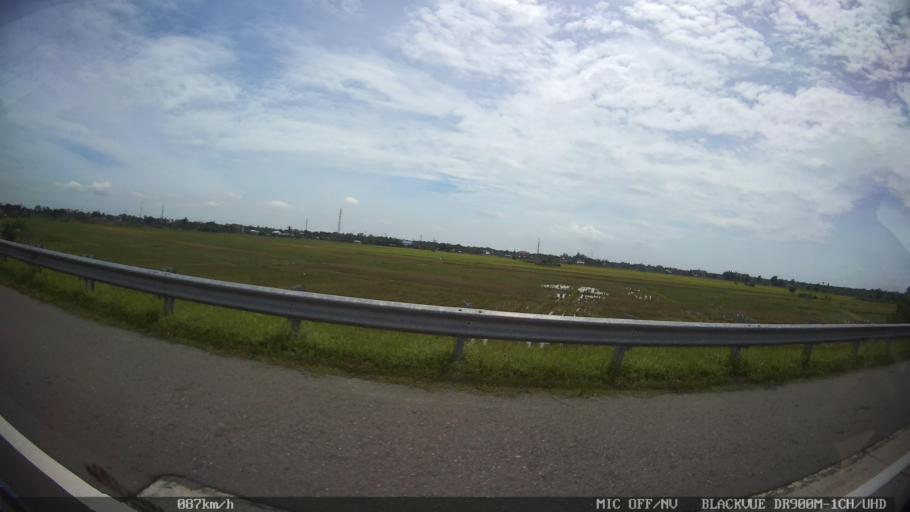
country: ID
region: North Sumatra
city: Percut
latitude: 3.5459
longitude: 98.8536
